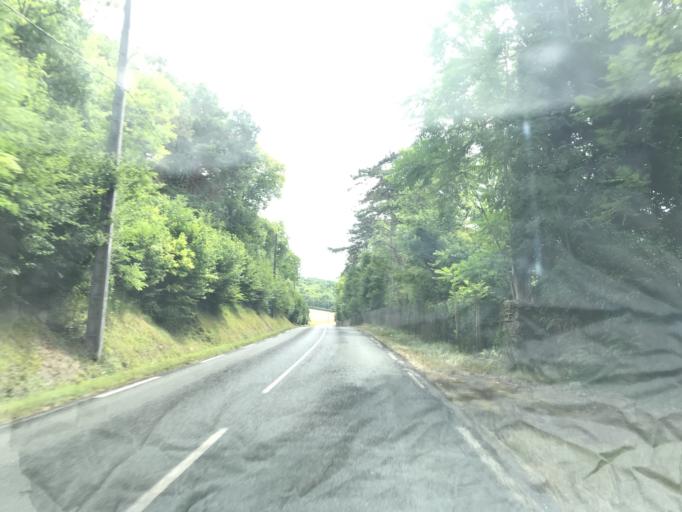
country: FR
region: Haute-Normandie
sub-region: Departement de l'Eure
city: Houlbec-Cocherel
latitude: 49.0628
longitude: 1.3250
